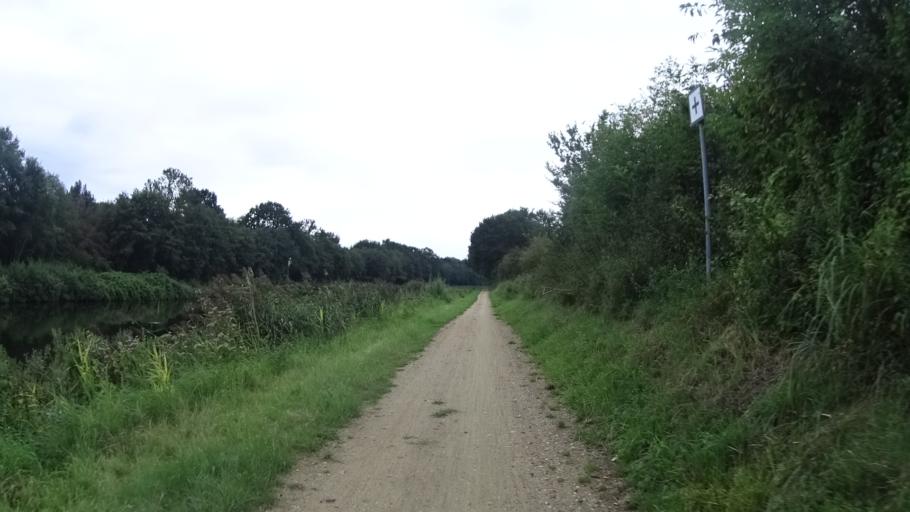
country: DE
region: Schleswig-Holstein
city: Molln
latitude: 53.6180
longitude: 10.6732
